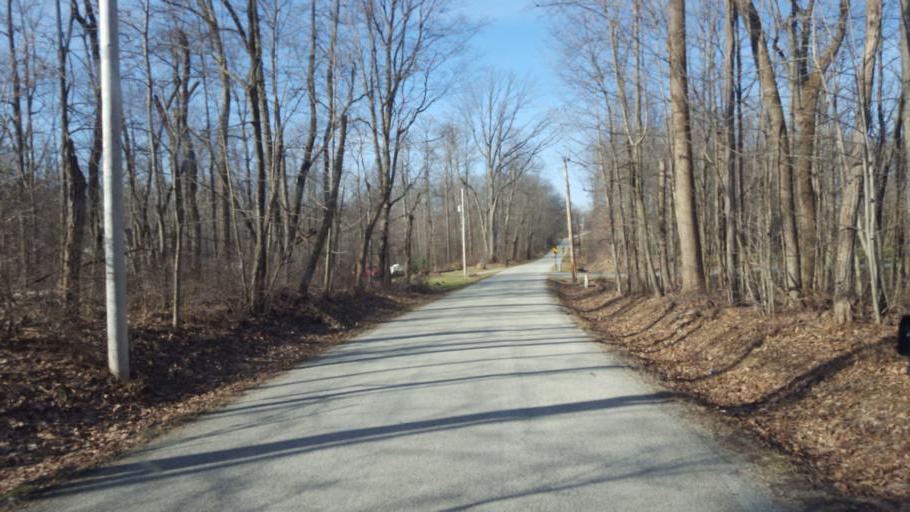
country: US
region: Ohio
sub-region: Morrow County
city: Mount Gilead
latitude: 40.5811
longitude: -82.7189
